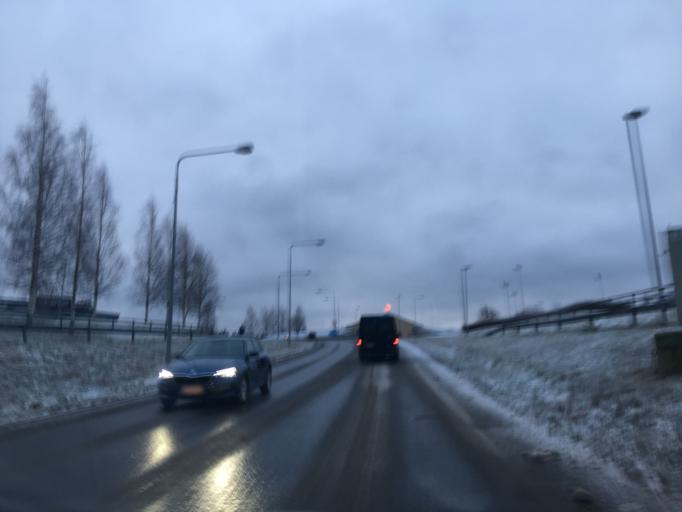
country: FI
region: Varsinais-Suomi
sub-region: Loimaa
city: Aura
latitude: 60.6476
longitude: 22.5894
